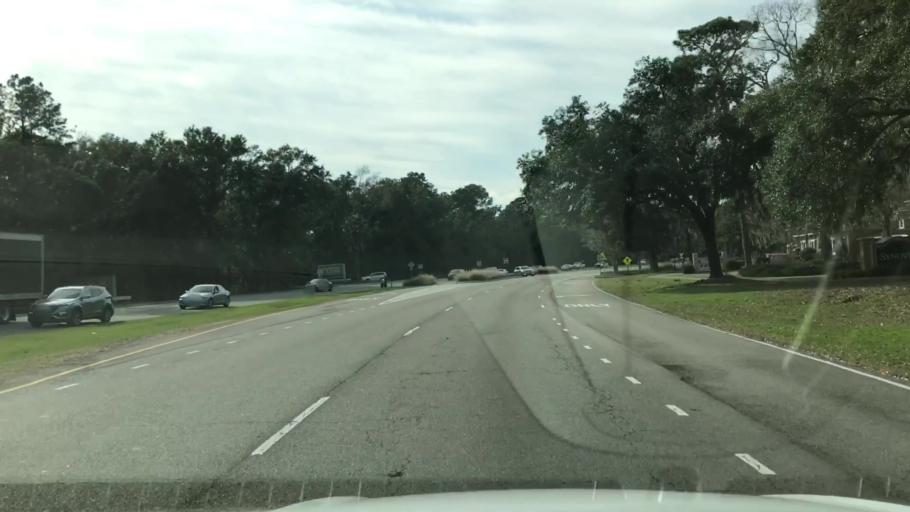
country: US
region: South Carolina
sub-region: Beaufort County
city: Hilton Head Island
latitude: 32.2129
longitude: -80.7246
